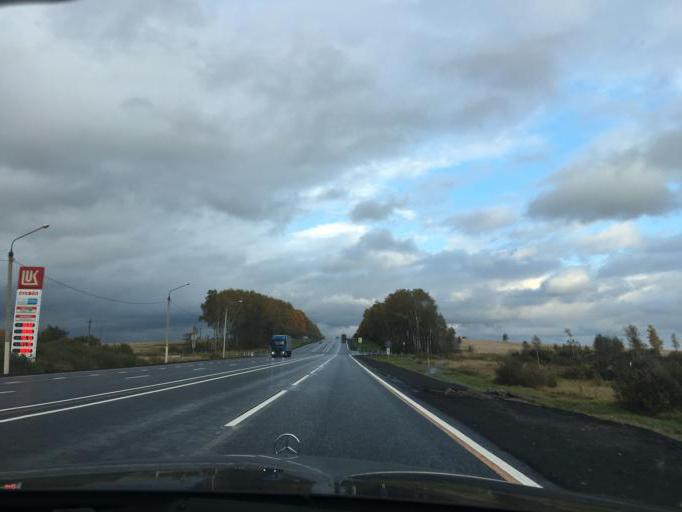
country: RU
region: Smolensk
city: Katyn'
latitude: 54.8492
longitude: 31.8037
